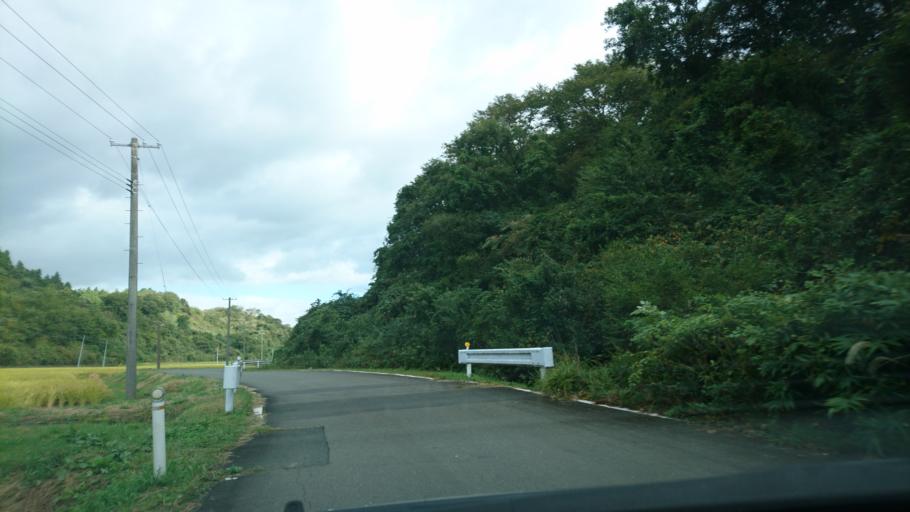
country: JP
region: Iwate
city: Ichinoseki
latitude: 38.8766
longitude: 141.0935
